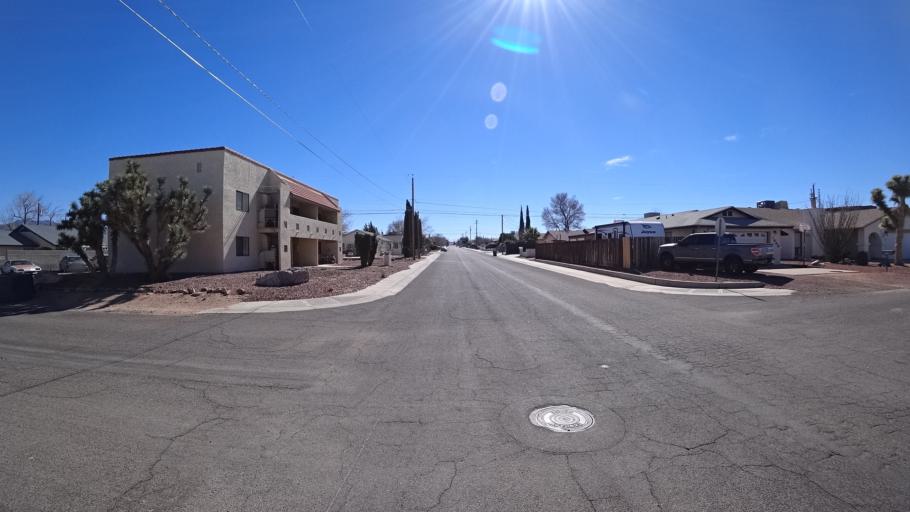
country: US
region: Arizona
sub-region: Mohave County
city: Kingman
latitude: 35.2039
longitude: -114.0313
